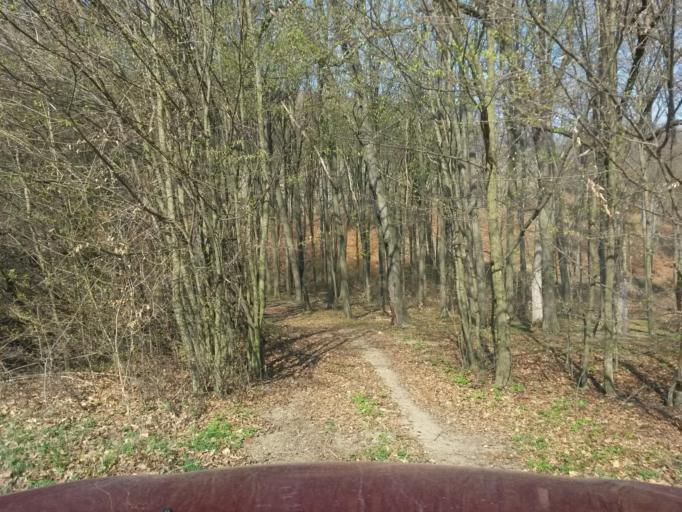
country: SK
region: Presovsky
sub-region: Okres Presov
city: Presov
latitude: 48.9293
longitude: 21.1476
